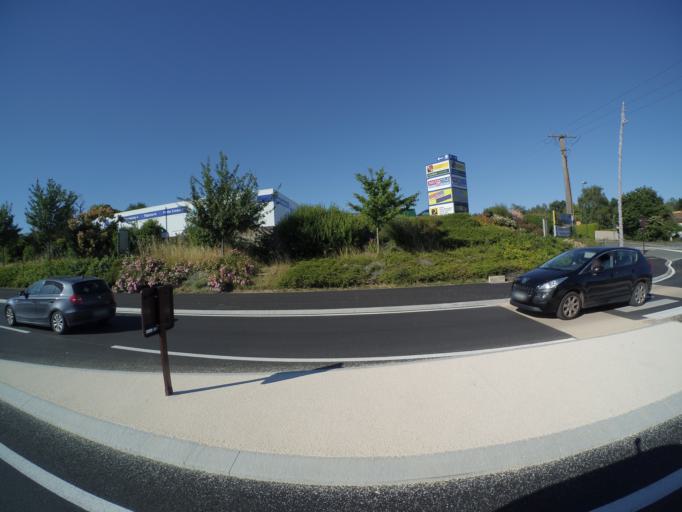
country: FR
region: Pays de la Loire
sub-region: Departement de la Vendee
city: Les Herbiers
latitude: 46.8761
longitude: -1.0271
